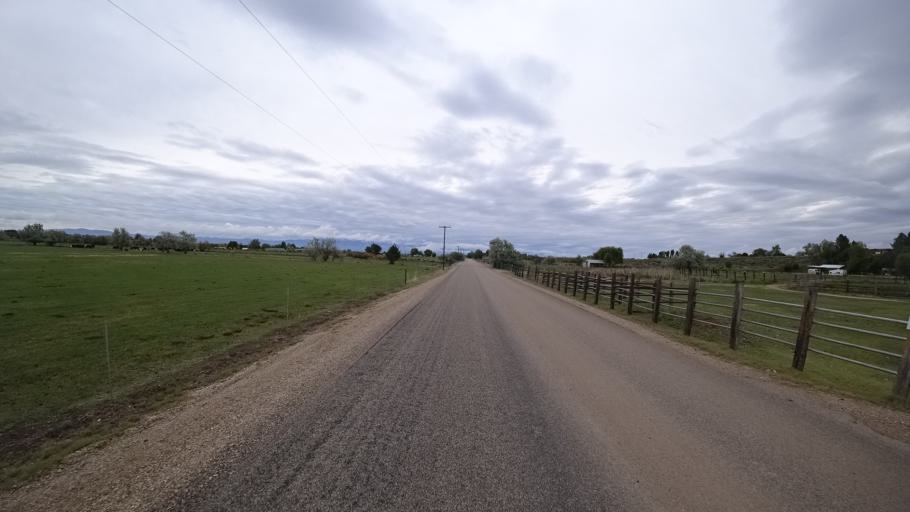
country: US
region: Idaho
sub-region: Ada County
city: Star
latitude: 43.6704
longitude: -116.5004
